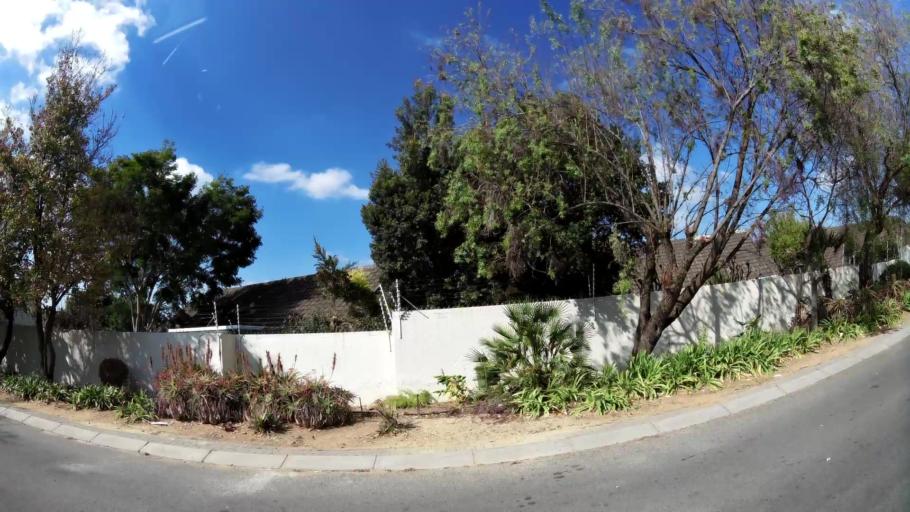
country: ZA
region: Gauteng
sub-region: West Rand District Municipality
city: Muldersdriseloop
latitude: -26.0697
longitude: 27.9461
